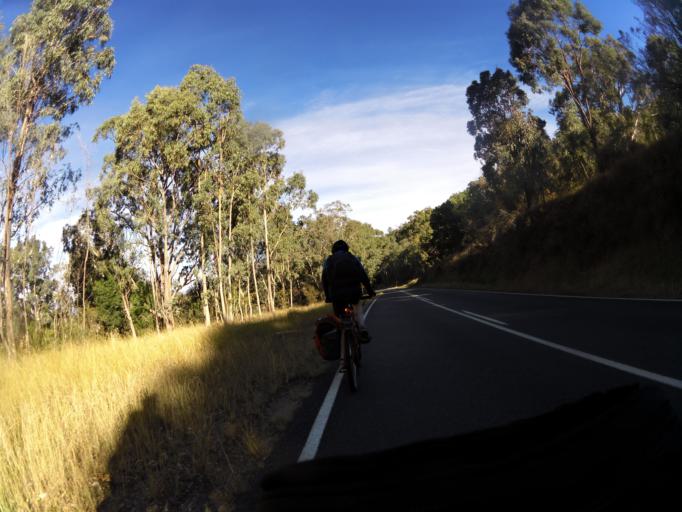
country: AU
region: New South Wales
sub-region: Greater Hume Shire
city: Holbrook
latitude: -35.9772
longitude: 147.8134
